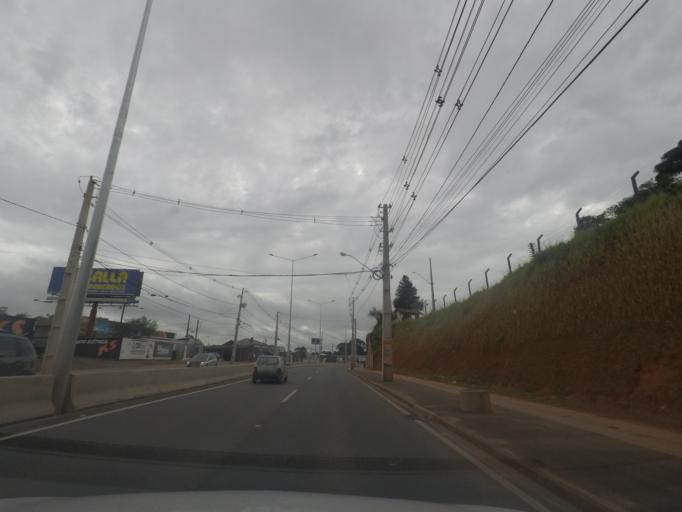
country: BR
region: Parana
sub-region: Piraquara
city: Piraquara
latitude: -25.4575
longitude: -49.0790
